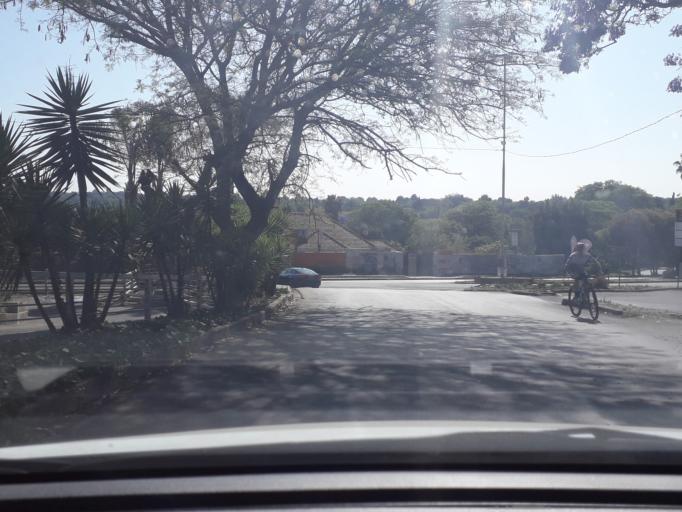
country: ZA
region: Gauteng
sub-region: City of Johannesburg Metropolitan Municipality
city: Johannesburg
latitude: -26.1435
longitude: 27.9792
